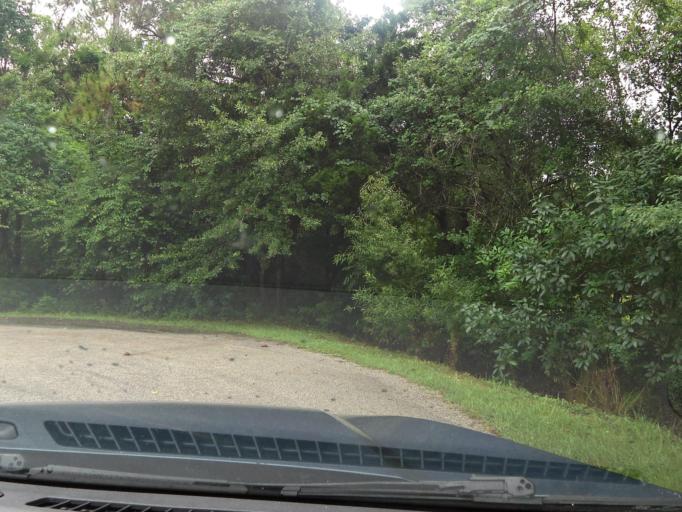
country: US
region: Florida
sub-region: Nassau County
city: Nassau Village-Ratliff
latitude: 30.5087
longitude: -81.8088
